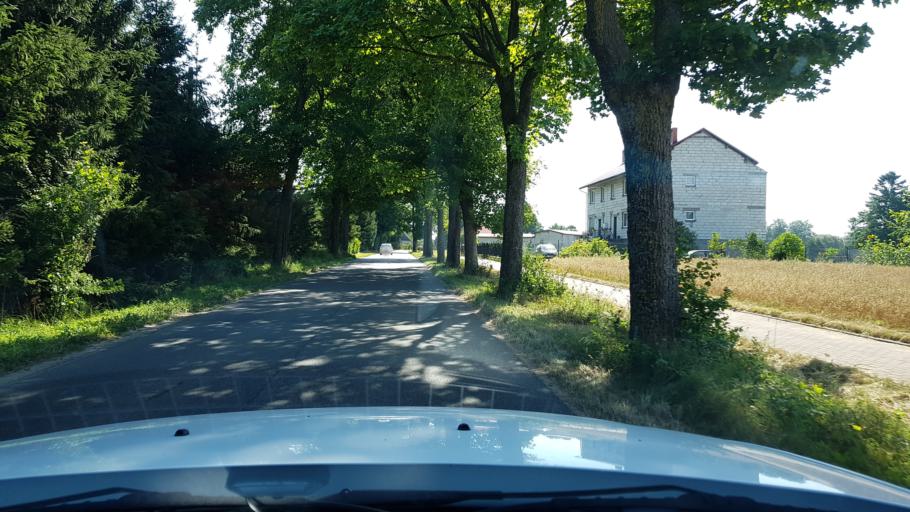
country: PL
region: West Pomeranian Voivodeship
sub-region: Powiat koszalinski
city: Sianow
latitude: 54.2726
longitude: 16.2332
